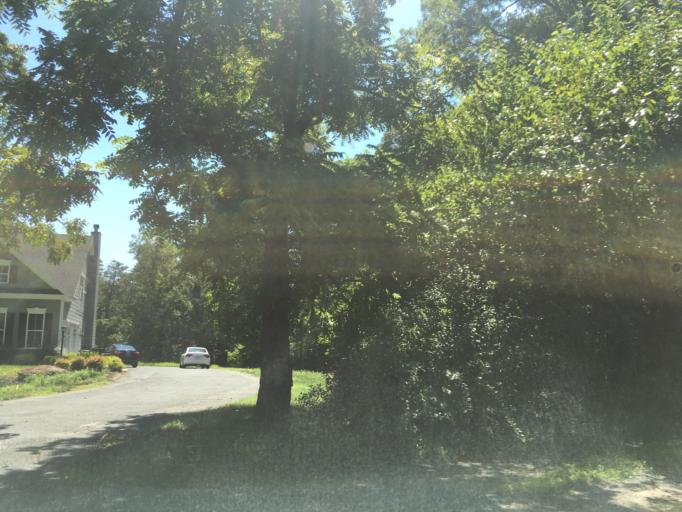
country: US
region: Maryland
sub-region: Anne Arundel County
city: Pasadena
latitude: 39.0885
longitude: -76.5636
